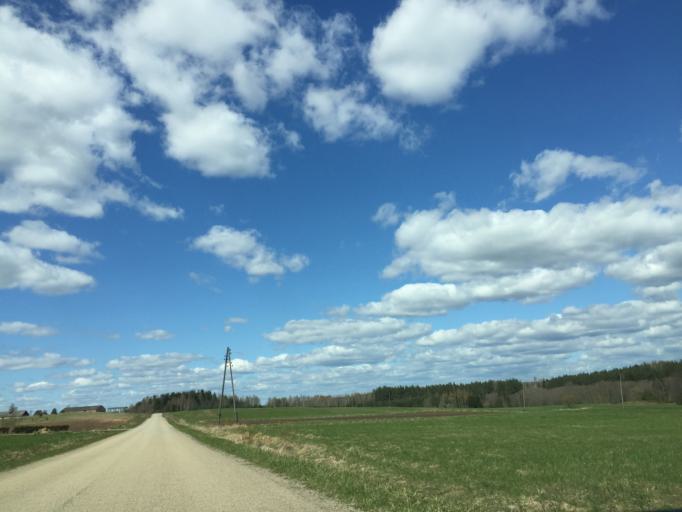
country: LV
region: Rezekne
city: Rezekne
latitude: 56.5693
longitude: 27.1378
